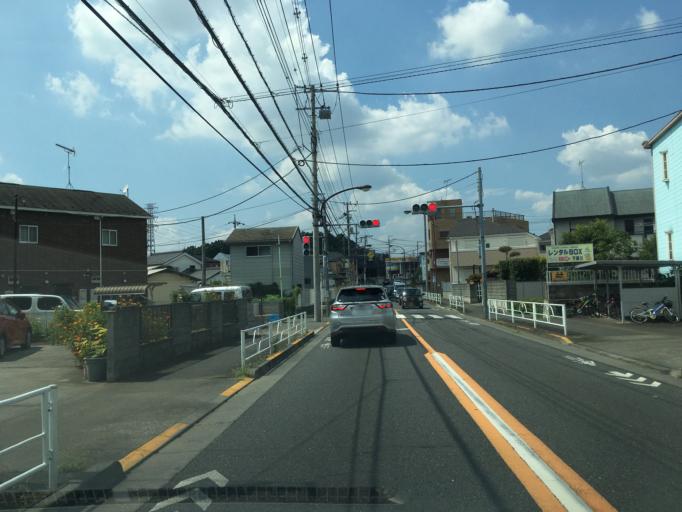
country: JP
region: Tokyo
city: Higashimurayama-shi
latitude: 35.7584
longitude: 139.5021
